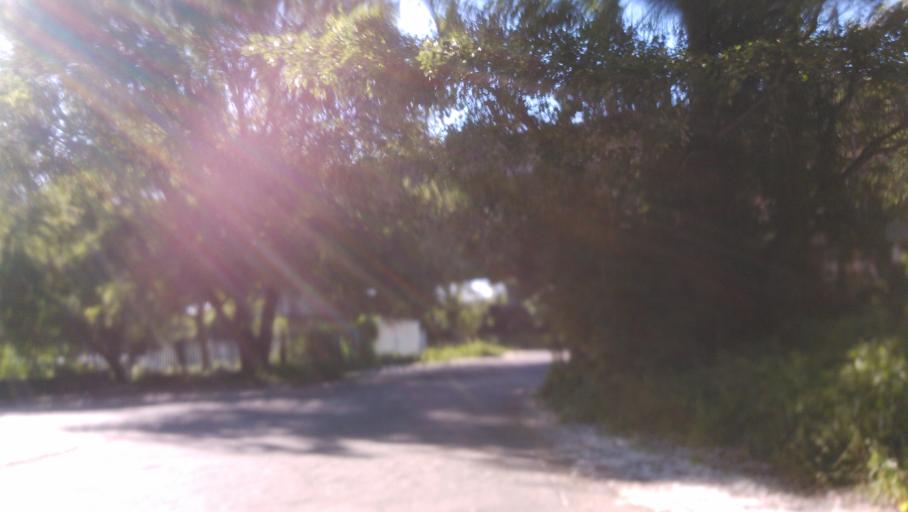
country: SK
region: Bratislavsky
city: Bratislava
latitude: 48.1306
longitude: 17.1351
